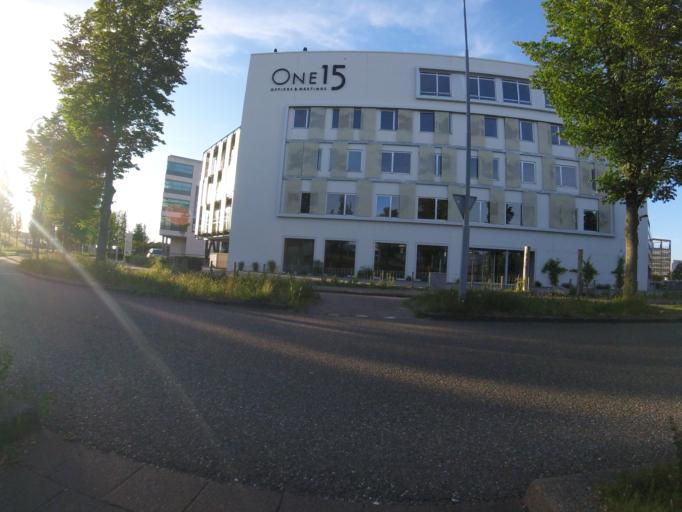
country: NL
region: North Holland
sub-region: Gemeente Haarlemmermeer
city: Hoofddorp
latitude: 52.2918
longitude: 4.7048
